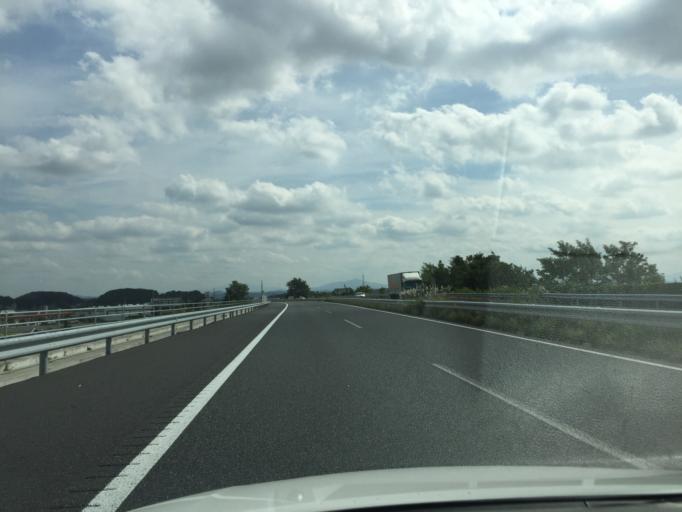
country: JP
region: Fukushima
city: Motomiya
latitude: 37.4610
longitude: 140.3738
